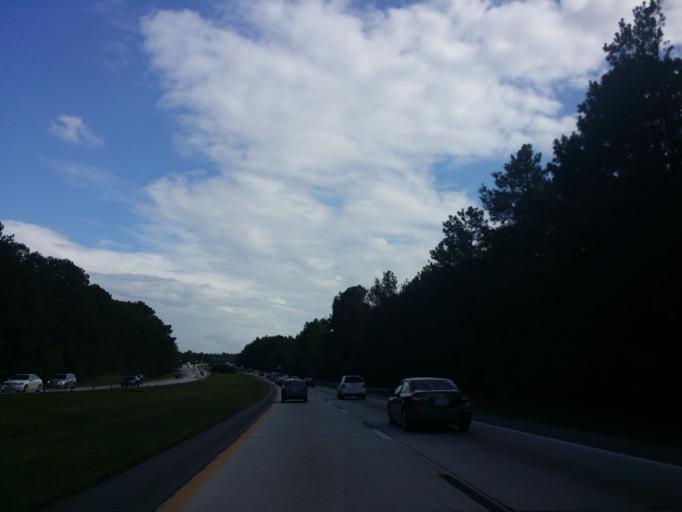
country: US
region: North Carolina
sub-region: Durham County
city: Durham
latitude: 35.9477
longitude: -78.8636
